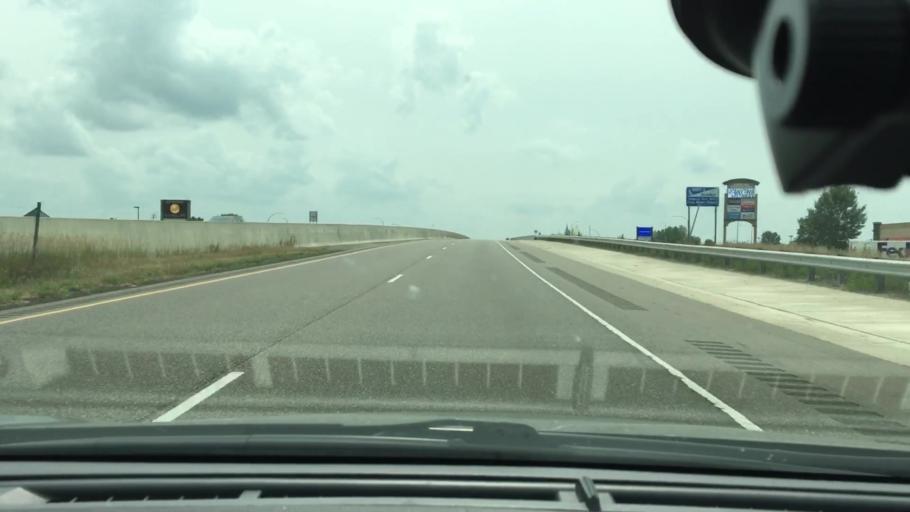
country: US
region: Minnesota
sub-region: Hennepin County
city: Rogers
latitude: 45.2125
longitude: -93.5527
